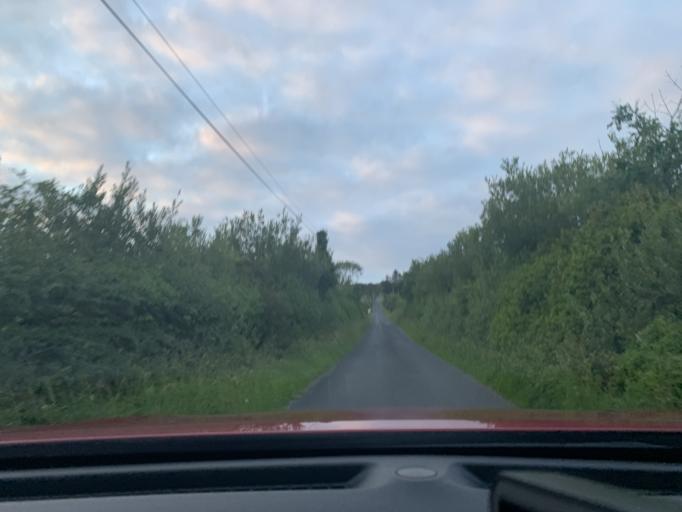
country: IE
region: Connaught
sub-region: Sligo
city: Sligo
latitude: 54.3553
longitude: -8.5063
